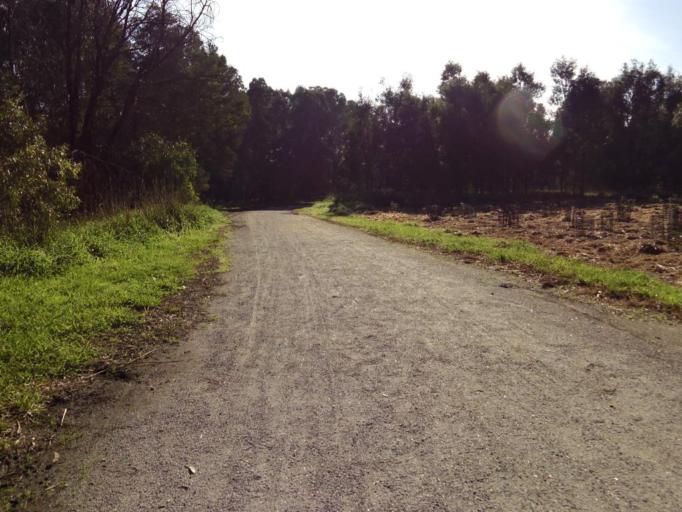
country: AU
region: Victoria
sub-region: Kingston
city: Dingley Village
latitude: -37.9904
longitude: 145.1209
